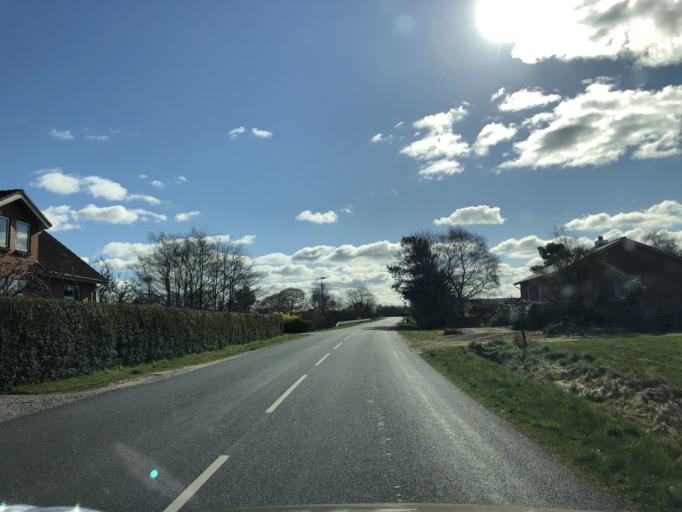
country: DK
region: North Denmark
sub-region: Vesthimmerland Kommune
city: Alestrup
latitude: 56.6068
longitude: 9.5525
